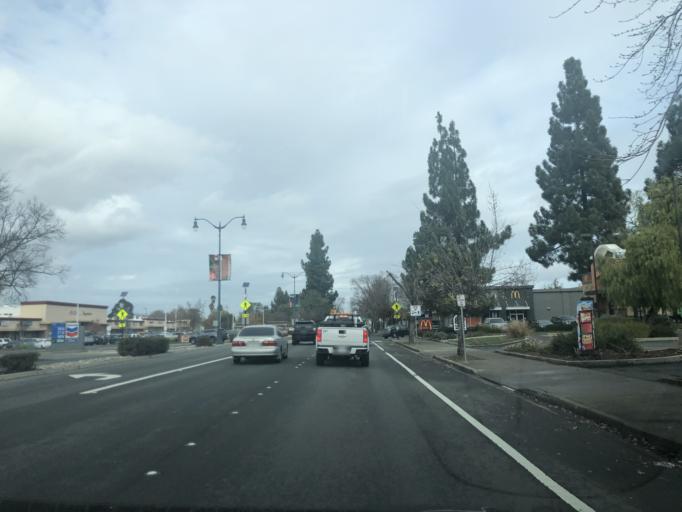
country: US
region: California
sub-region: Contra Costa County
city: Pleasant Hill
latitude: 37.9527
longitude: -122.0601
